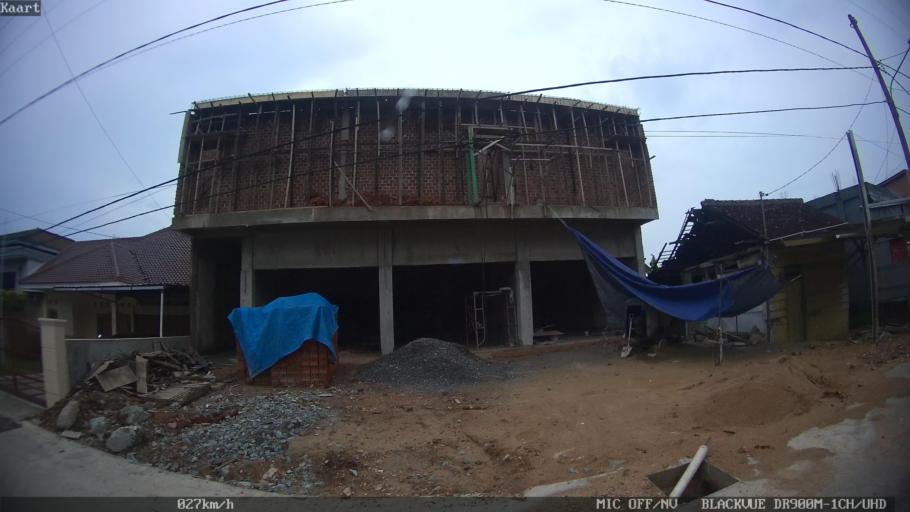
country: ID
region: Lampung
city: Kedaton
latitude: -5.3775
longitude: 105.2460
